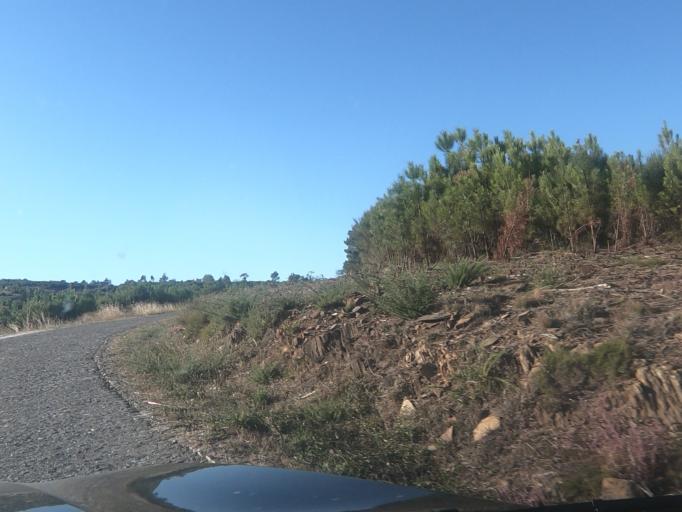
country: PT
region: Vila Real
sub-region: Sabrosa
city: Sabrosa
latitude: 41.3228
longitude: -7.5885
